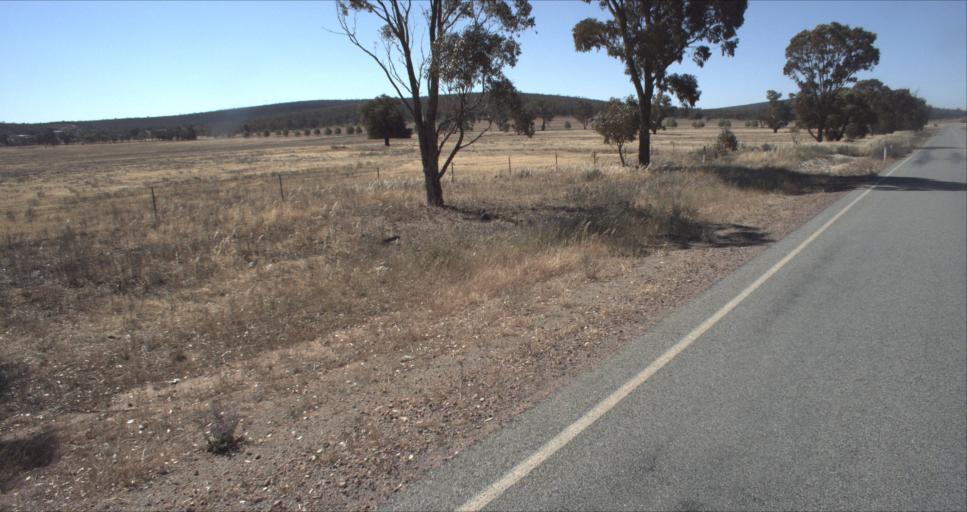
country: AU
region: New South Wales
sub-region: Leeton
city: Leeton
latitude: -34.4834
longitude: 146.4751
